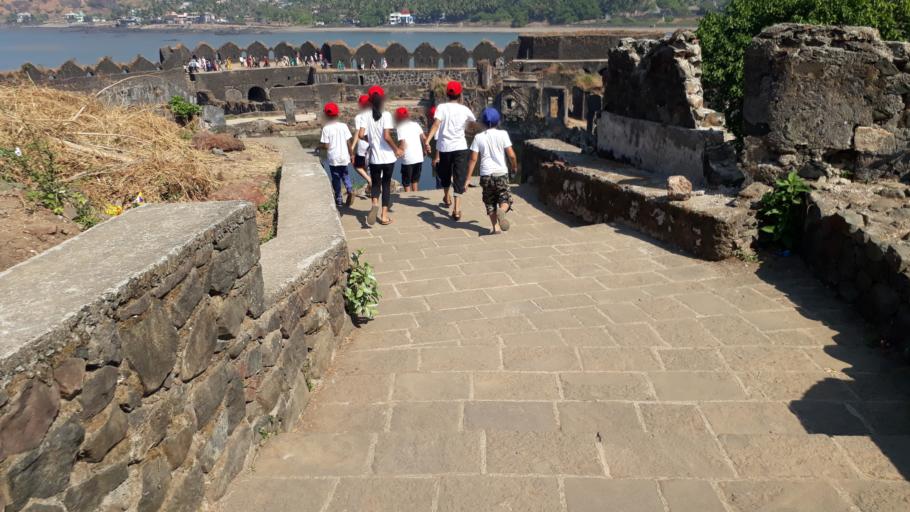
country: IN
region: Maharashtra
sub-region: Raigarh
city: Murud
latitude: 18.3002
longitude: 72.9645
